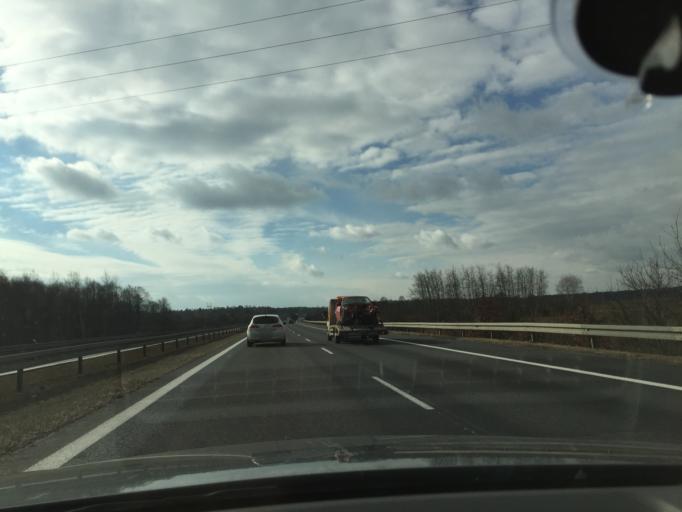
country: PL
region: Lodz Voivodeship
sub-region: Powiat radomszczanski
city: Kamiensk
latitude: 51.2568
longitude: 19.5282
